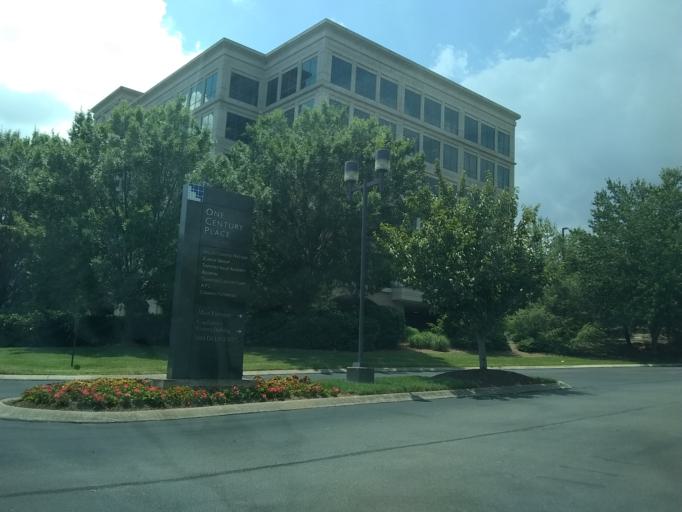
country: US
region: Tennessee
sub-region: Davidson County
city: Nashville
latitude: 36.1481
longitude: -86.6859
